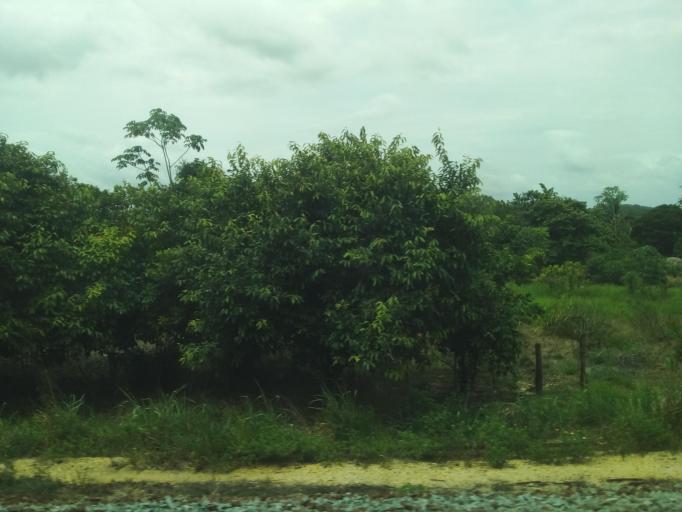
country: BR
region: Maranhao
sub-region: Santa Ines
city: Santa Ines
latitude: -3.7059
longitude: -45.9571
